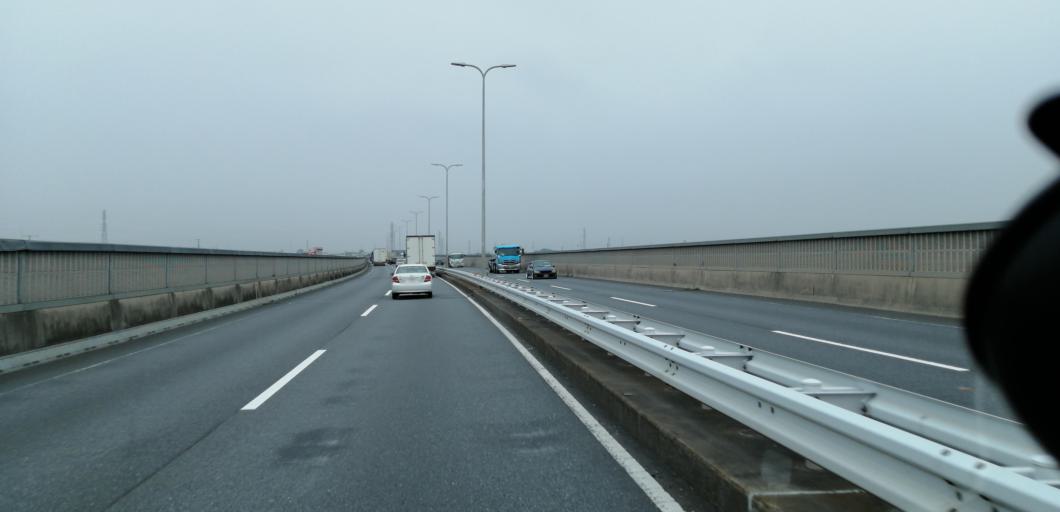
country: JP
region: Saitama
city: Kumagaya
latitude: 36.1652
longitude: 139.3899
